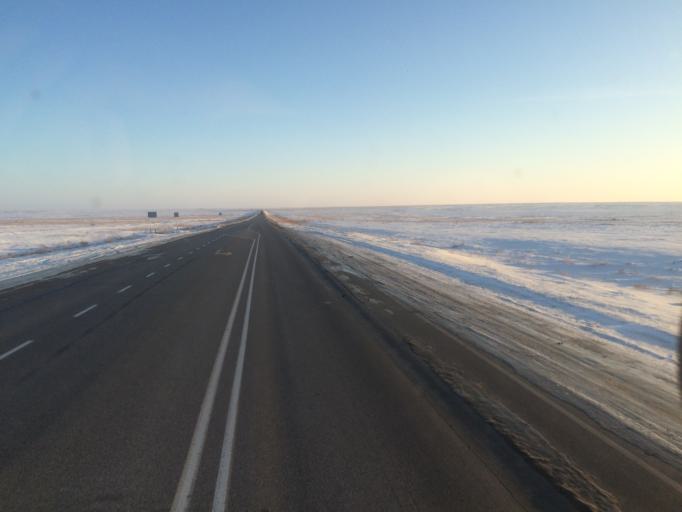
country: KZ
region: Aqtoebe
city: Yrghyz
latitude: 47.9105
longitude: 61.2989
